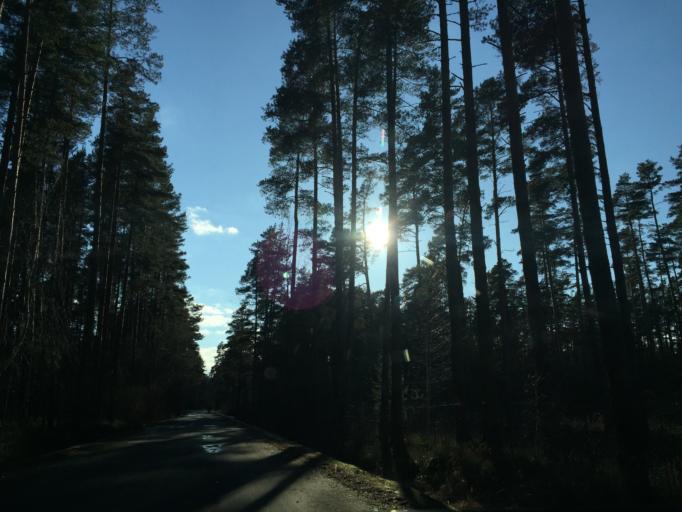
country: LV
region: Babite
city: Pinki
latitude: 56.9239
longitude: 23.8939
